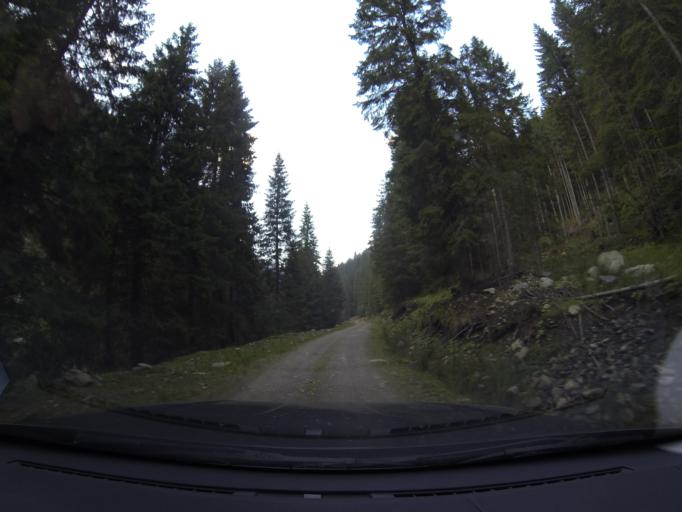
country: RO
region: Brasov
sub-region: Oras Victoria
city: Victoria
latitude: 45.5581
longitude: 24.6865
